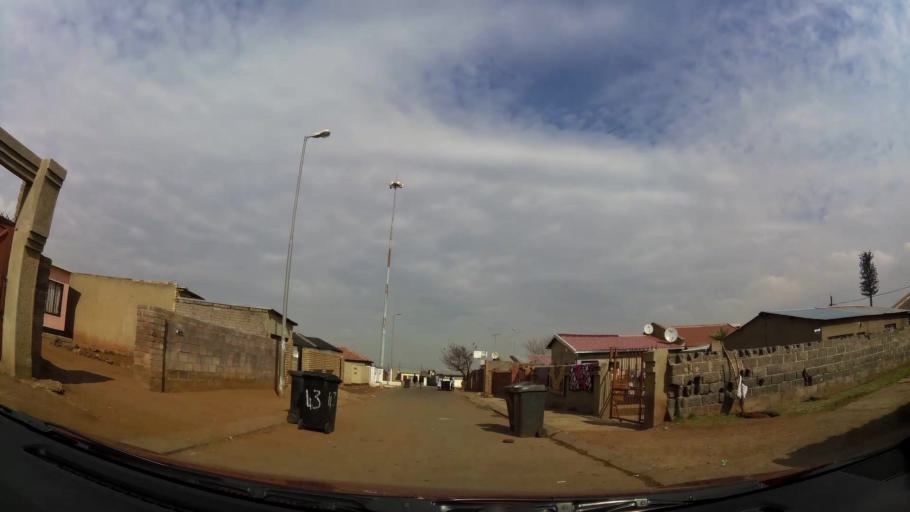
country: ZA
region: Gauteng
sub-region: City of Johannesburg Metropolitan Municipality
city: Soweto
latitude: -26.2570
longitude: 27.8180
